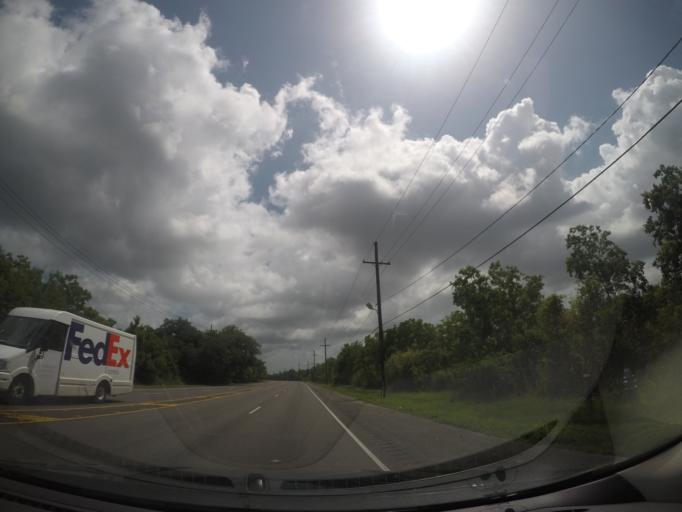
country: US
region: Louisiana
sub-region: Saint Bernard Parish
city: Meraux
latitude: 30.0594
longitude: -89.8692
